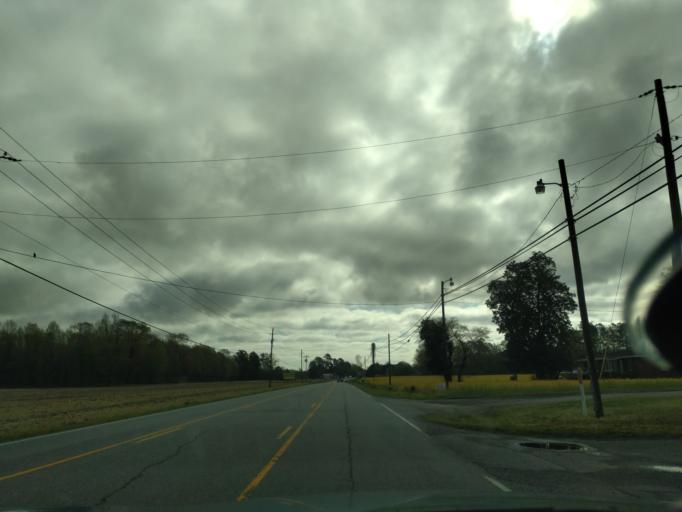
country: US
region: North Carolina
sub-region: Chowan County
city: Edenton
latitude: 36.0571
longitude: -76.6493
